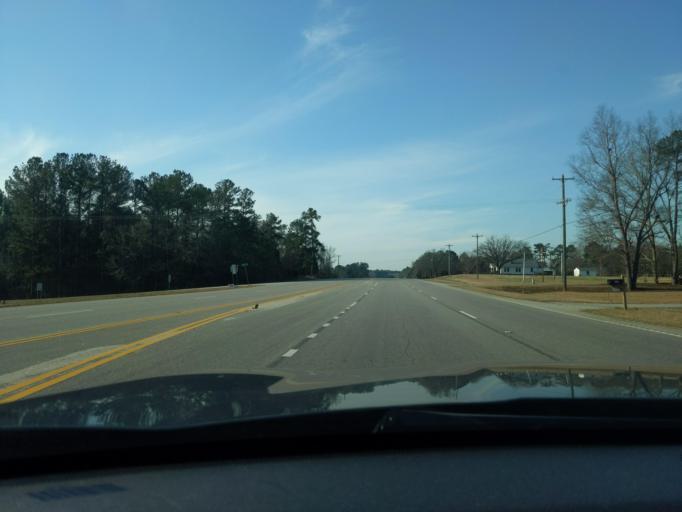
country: US
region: South Carolina
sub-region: Abbeville County
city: Abbeville
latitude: 34.1434
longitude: -82.4055
